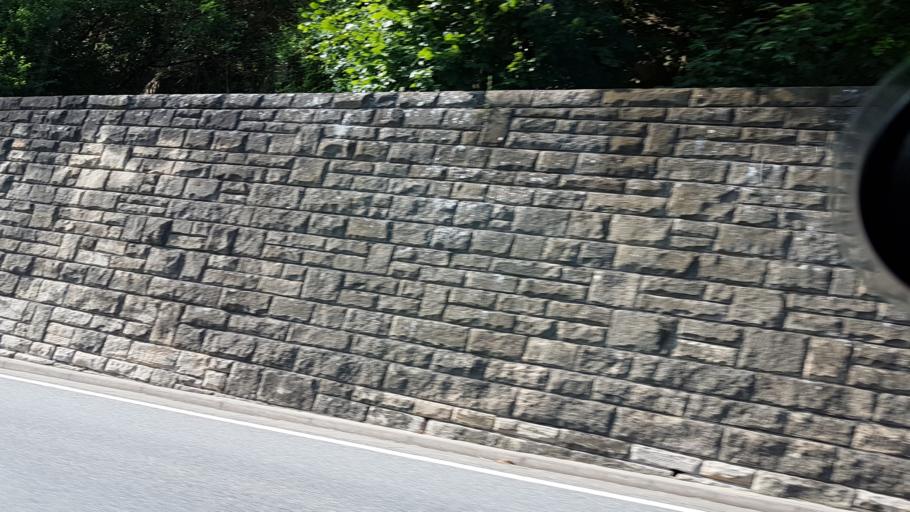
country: DE
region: Rheinland-Pfalz
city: Odenbach
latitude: 49.6802
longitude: 7.6397
